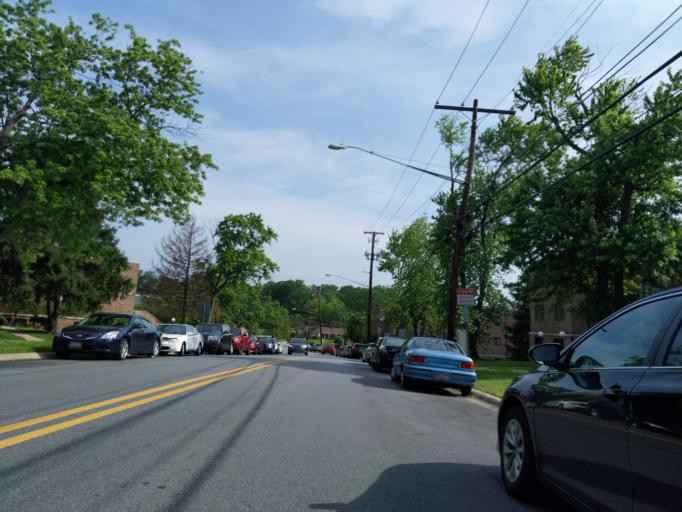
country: US
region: Maryland
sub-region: Montgomery County
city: Wheaton
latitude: 39.0436
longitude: -77.0478
